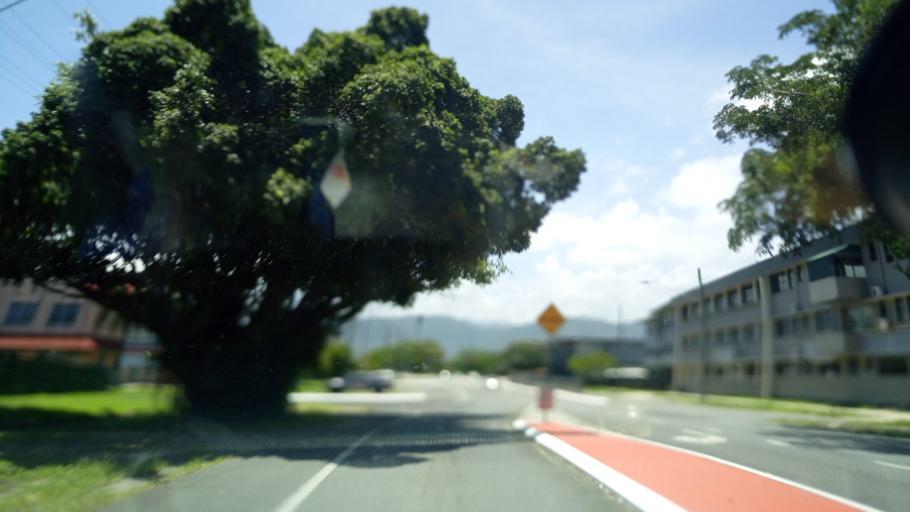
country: AU
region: Queensland
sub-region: Cairns
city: Cairns
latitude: -16.9271
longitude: 145.7689
